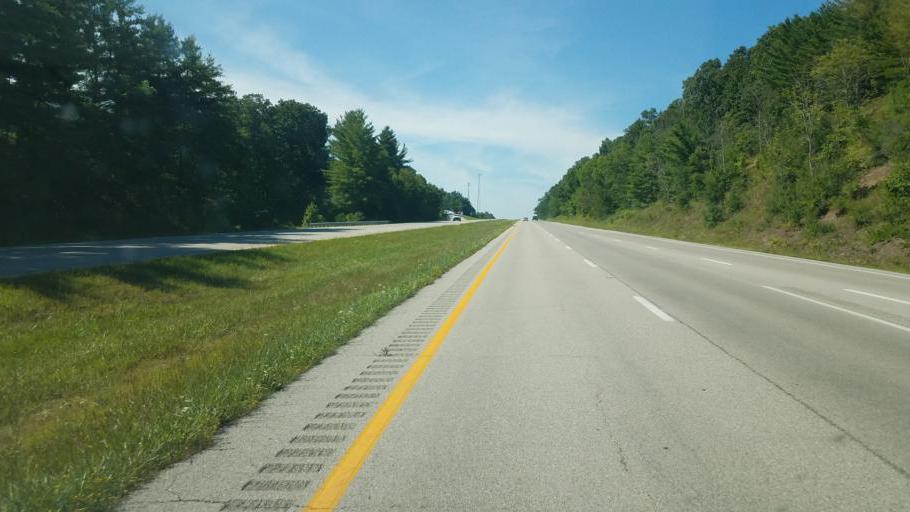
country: US
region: Ohio
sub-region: Meigs County
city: Pomeroy
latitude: 39.1210
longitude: -82.0173
